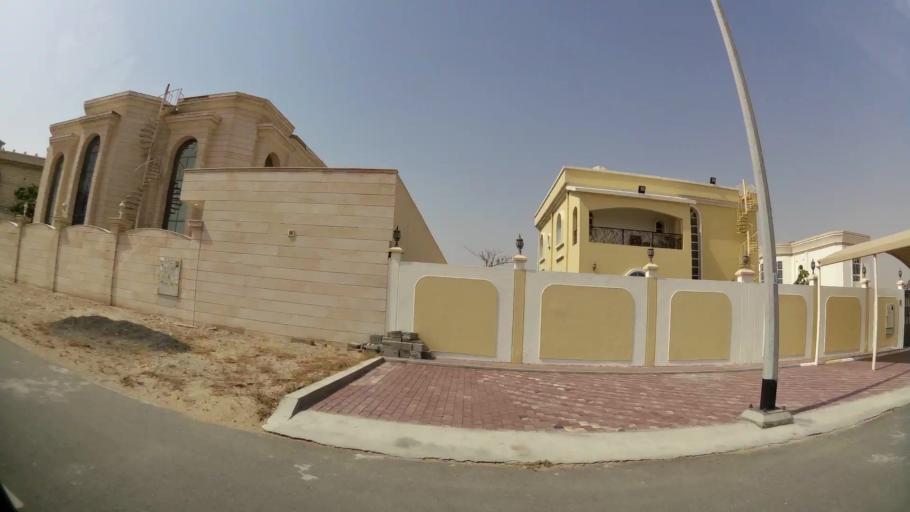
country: AE
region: Ash Shariqah
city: Sharjah
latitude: 25.2517
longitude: 55.4473
